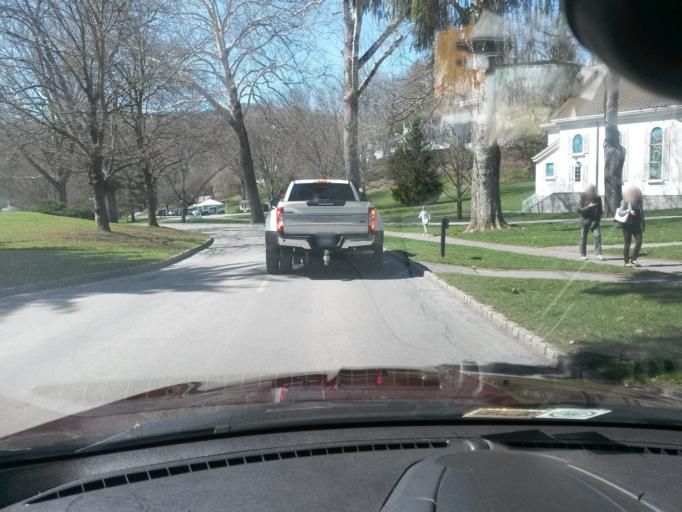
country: US
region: West Virginia
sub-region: Greenbrier County
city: White Sulphur Springs
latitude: 37.7873
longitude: -80.3106
